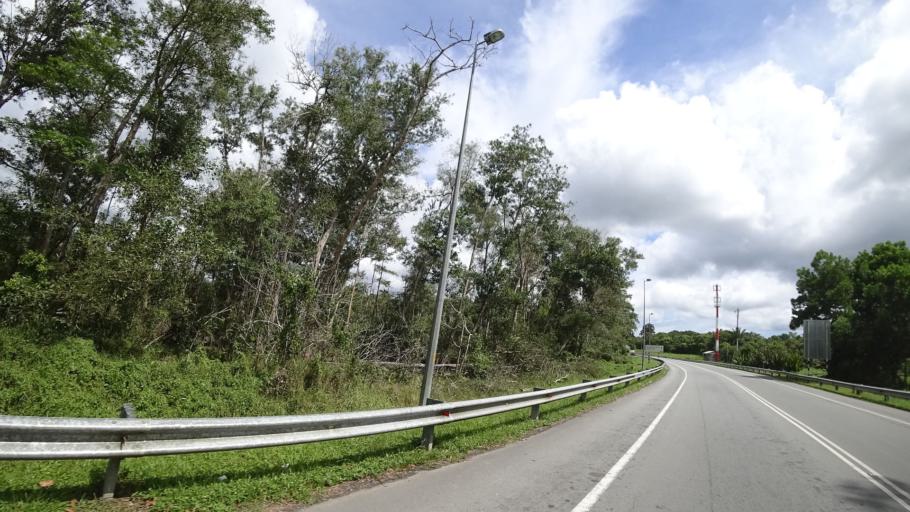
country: BN
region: Tutong
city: Tutong
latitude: 4.7443
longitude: 114.8147
